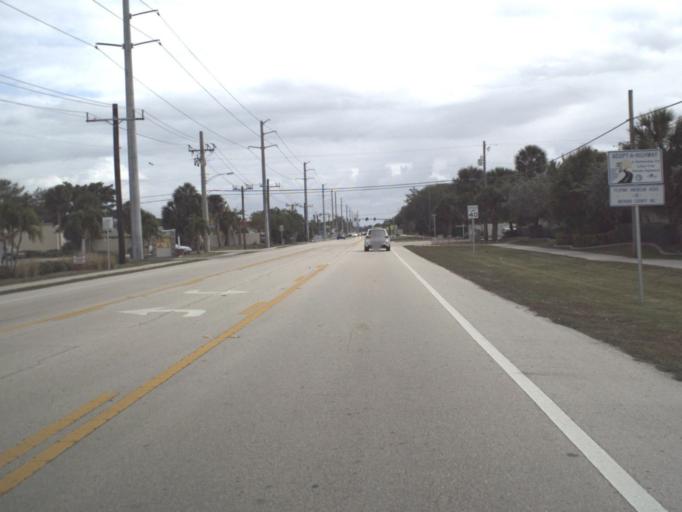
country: US
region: Florida
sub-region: Brevard County
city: Satellite Beach
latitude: 28.1758
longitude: -80.6061
